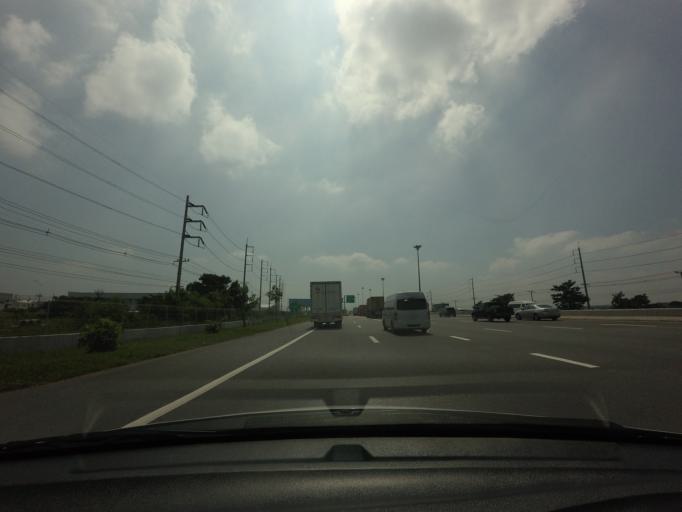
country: TH
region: Chachoengsao
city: Bang Pakong
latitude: 13.5635
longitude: 100.9888
